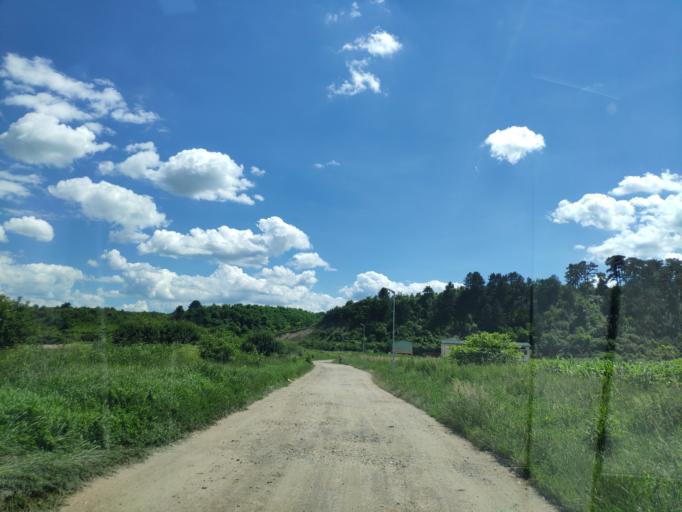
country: HU
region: Borsod-Abauj-Zemplen
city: Arlo
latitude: 48.2788
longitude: 20.1920
